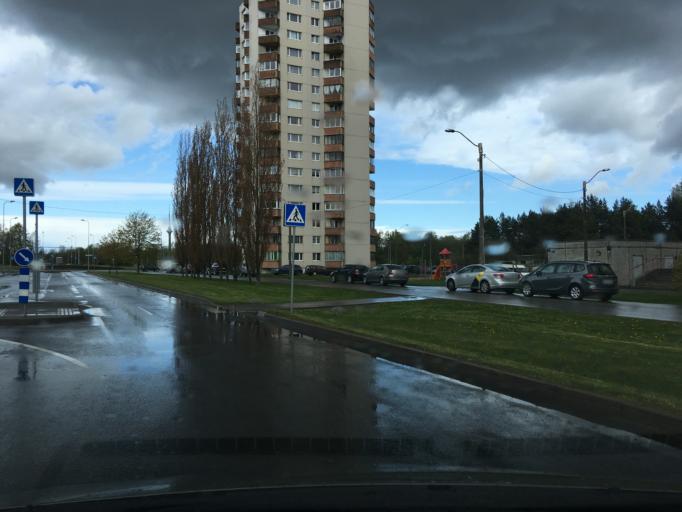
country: EE
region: Harju
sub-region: Tallinna linn
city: Kose
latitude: 59.4452
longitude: 24.8988
